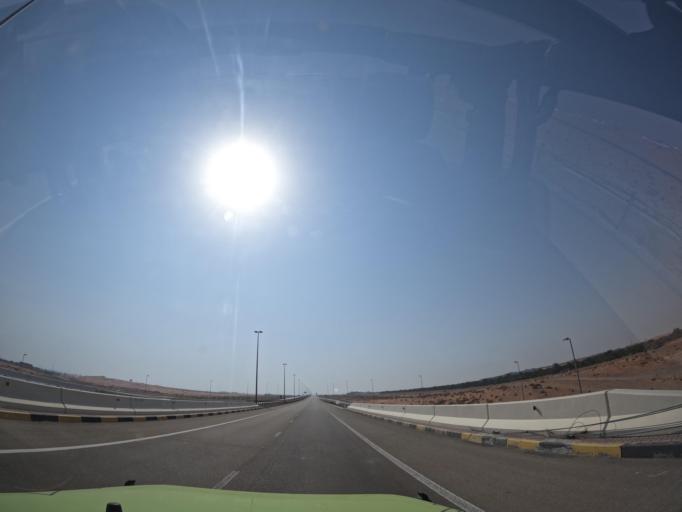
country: OM
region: Al Buraimi
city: Al Buraymi
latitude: 24.4084
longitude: 55.7046
